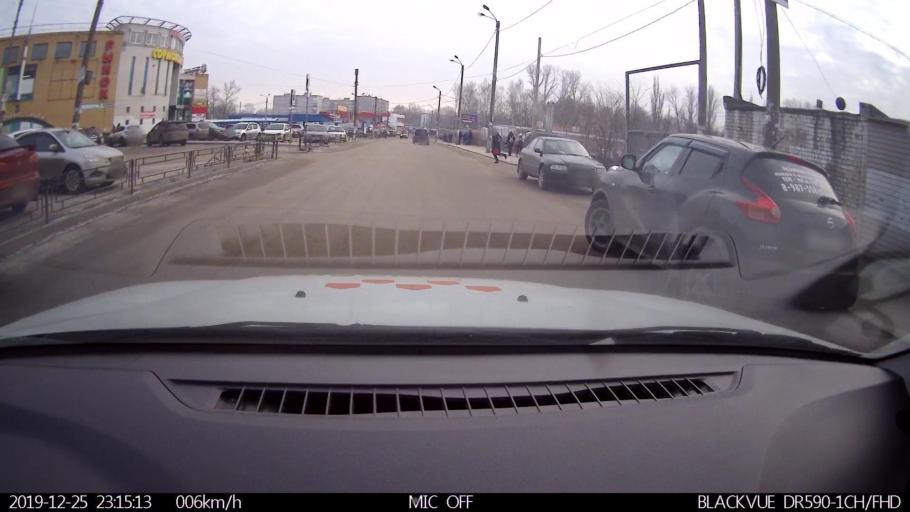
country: RU
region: Nizjnij Novgorod
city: Gorbatovka
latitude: 56.3604
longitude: 43.8242
